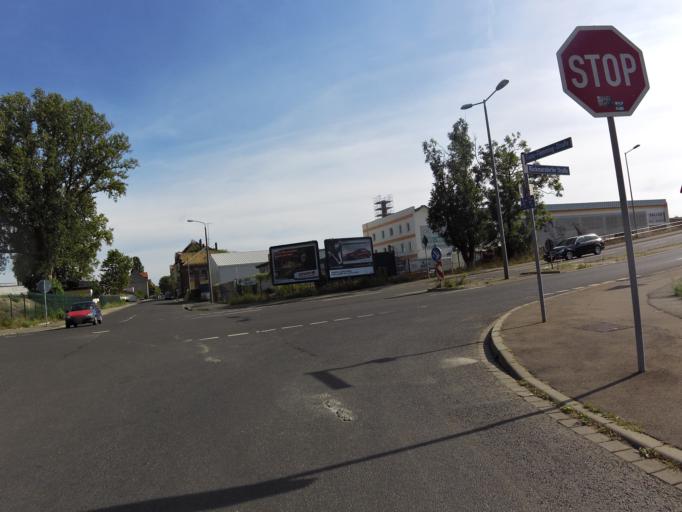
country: DE
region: Saxony
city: Leipzig
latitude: 51.3466
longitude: 12.3068
